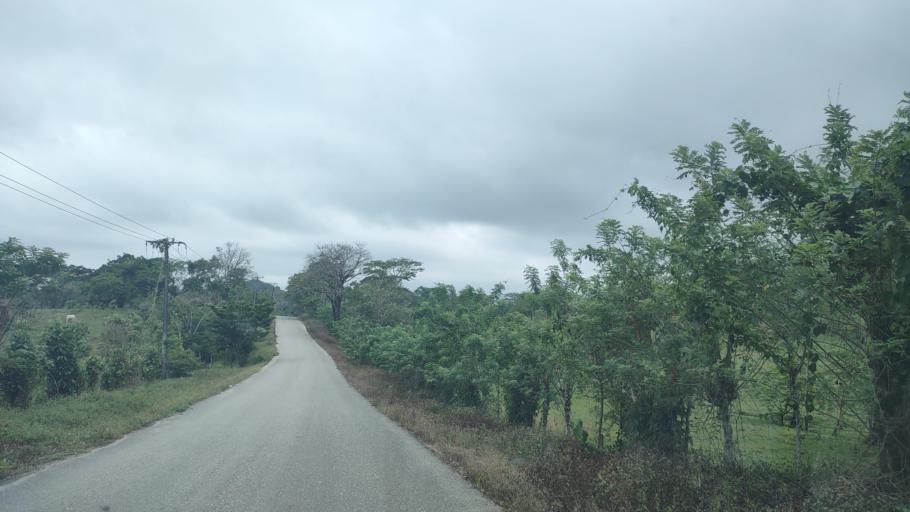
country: MX
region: Veracruz
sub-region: Uxpanapa
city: Poblado 10
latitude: 17.4797
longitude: -94.1201
